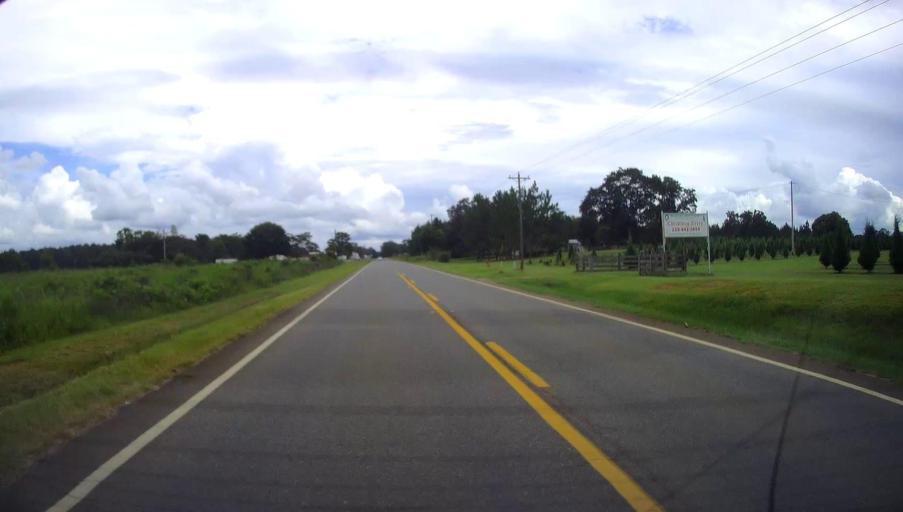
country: US
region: Georgia
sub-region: Schley County
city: Ellaville
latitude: 32.2520
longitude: -84.3348
